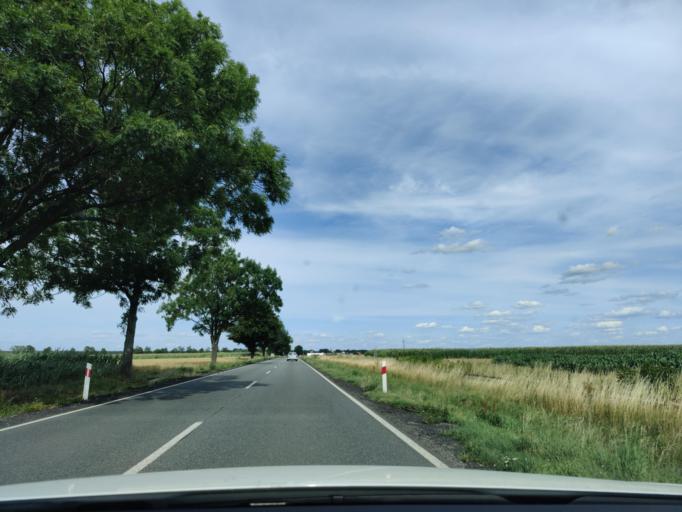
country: PL
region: Opole Voivodeship
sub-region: Powiat krapkowicki
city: Strzeleczki
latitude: 50.4515
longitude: 17.8306
